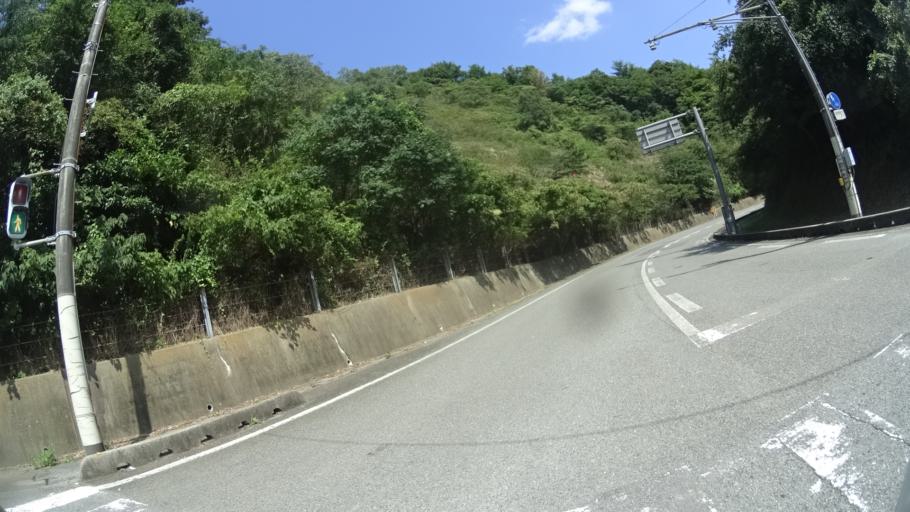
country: JP
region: Shimane
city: Masuda
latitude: 34.6228
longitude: 131.6089
